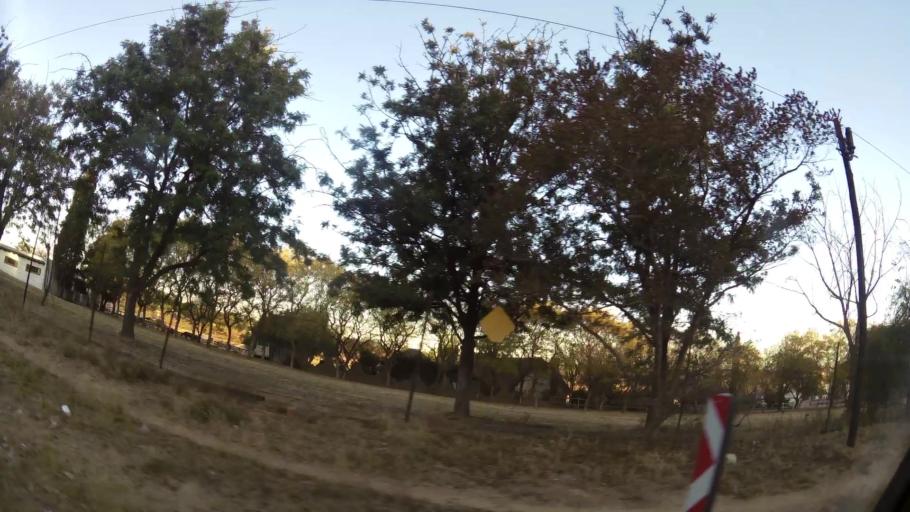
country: ZA
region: Gauteng
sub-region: City of Johannesburg Metropolitan Municipality
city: Diepsloot
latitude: -25.9462
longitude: 28.0529
